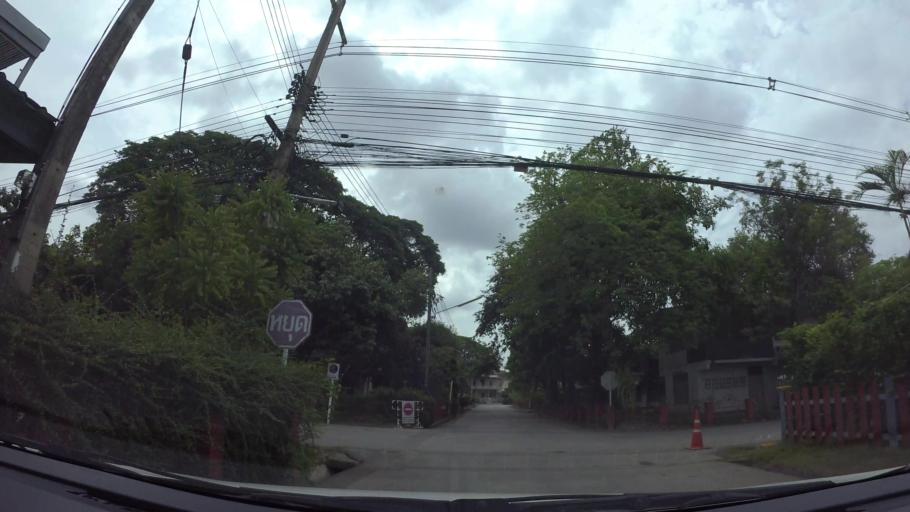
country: TH
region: Chiang Mai
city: Chiang Mai
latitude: 18.7879
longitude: 98.9753
